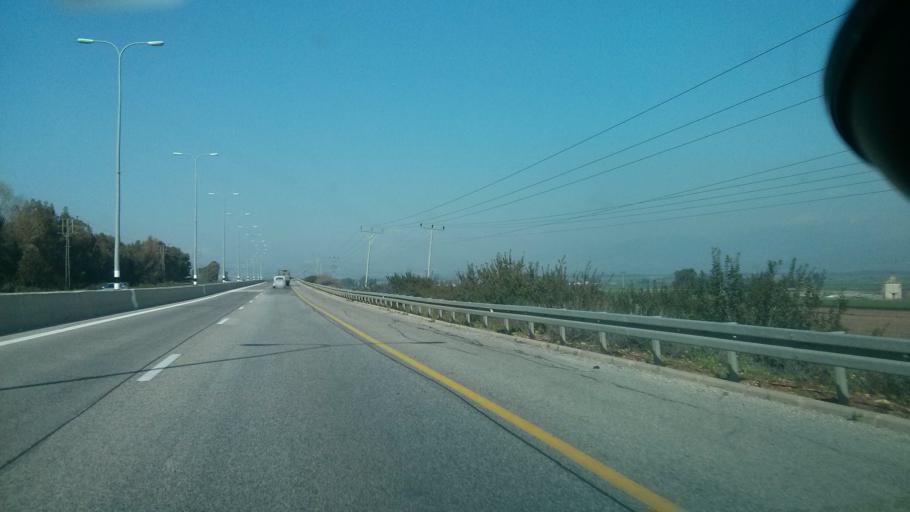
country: IL
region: Northern District
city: Qiryat Shemona
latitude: 33.0892
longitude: 35.5750
